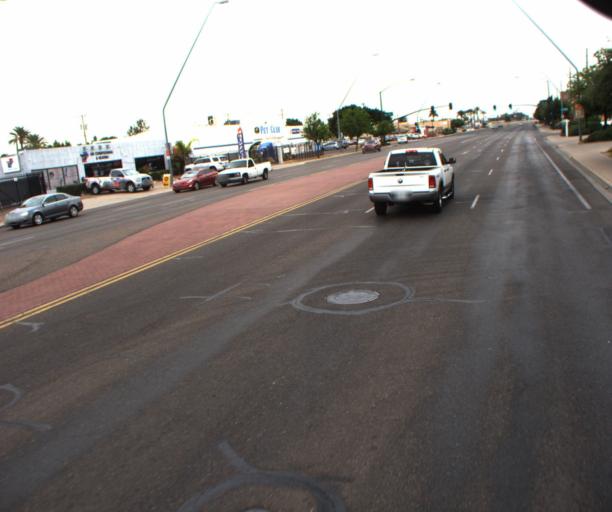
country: US
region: Arizona
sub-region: Maricopa County
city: Mesa
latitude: 33.4142
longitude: -111.8400
